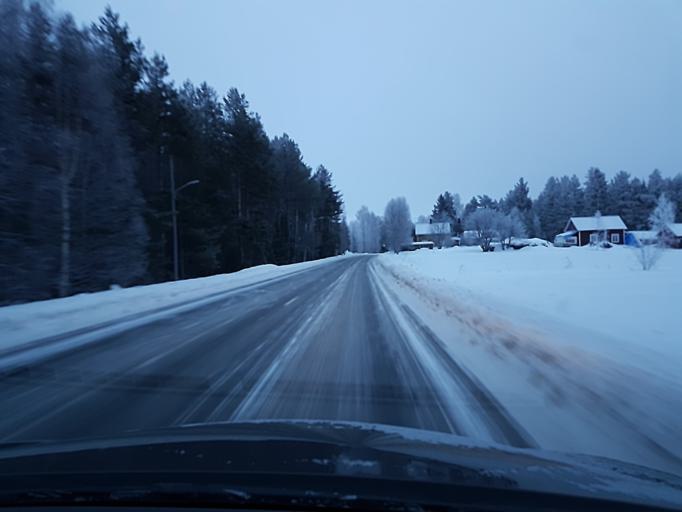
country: SE
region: Norrbotten
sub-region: Pitea Kommun
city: Roknas
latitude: 65.3474
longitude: 21.1161
